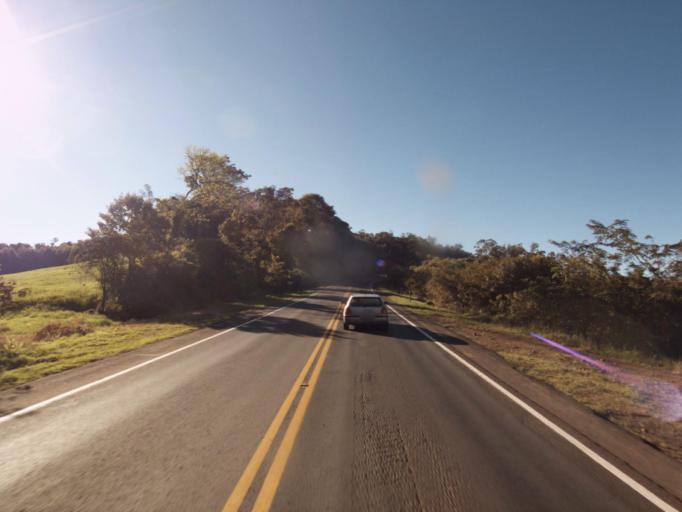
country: AR
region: Misiones
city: Bernardo de Irigoyen
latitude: -26.5087
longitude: -53.5130
